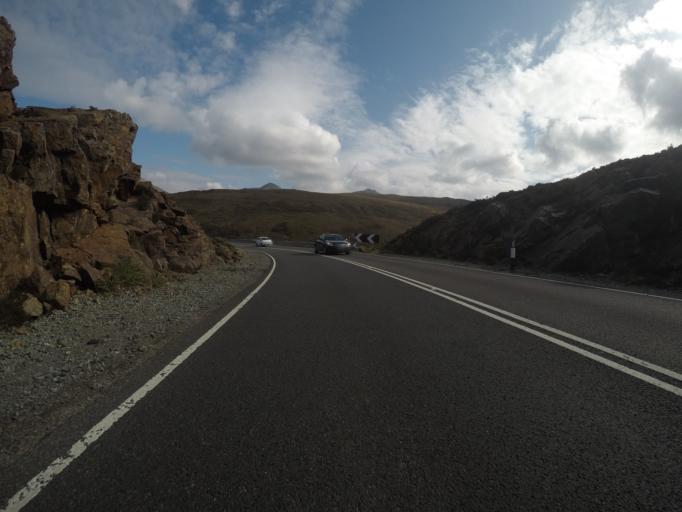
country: GB
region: Scotland
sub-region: Highland
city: Portree
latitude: 57.2742
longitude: -6.0989
